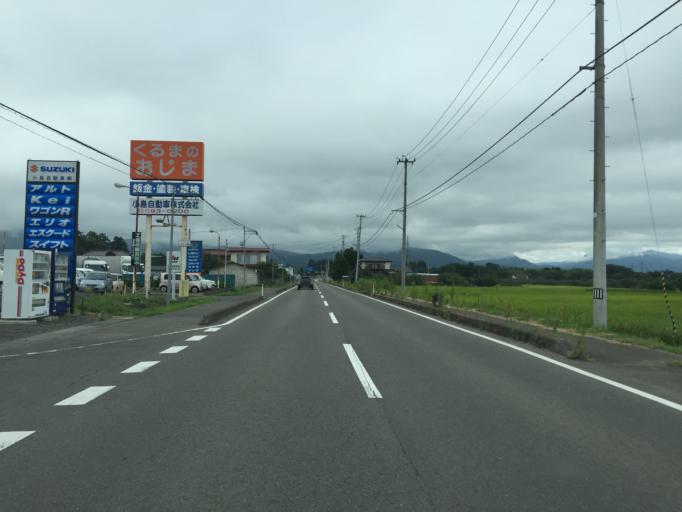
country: JP
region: Fukushima
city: Fukushima-shi
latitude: 37.7503
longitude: 140.4023
